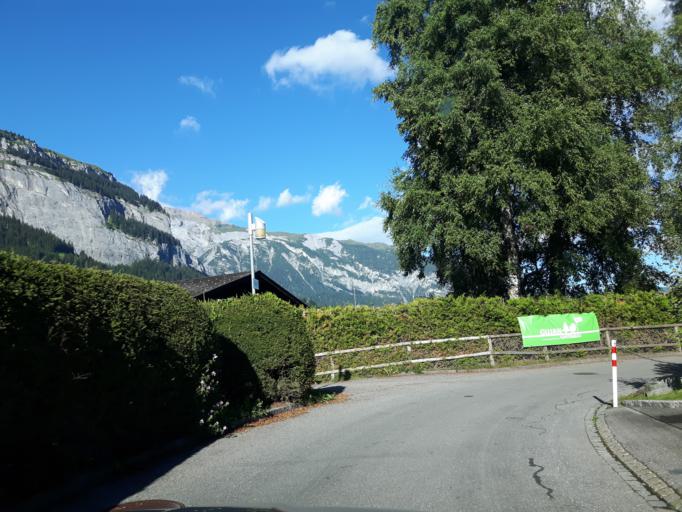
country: CH
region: Grisons
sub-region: Imboden District
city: Flims
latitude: 46.8321
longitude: 9.2832
